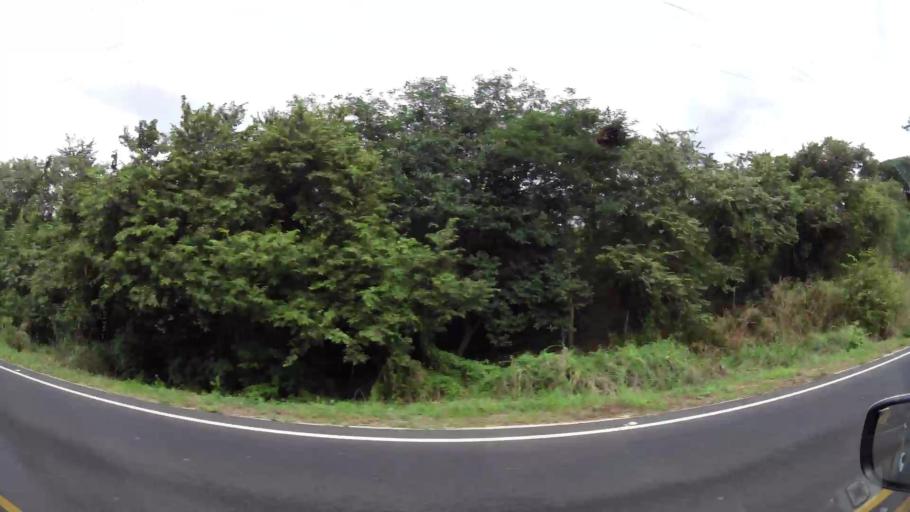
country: CR
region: Guanacaste
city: Nandayure
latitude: 10.2464
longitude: -85.2251
